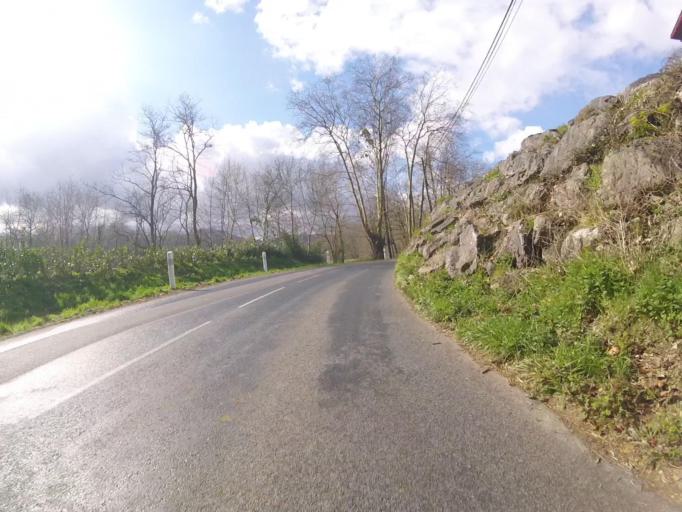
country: FR
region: Aquitaine
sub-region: Departement des Pyrenees-Atlantiques
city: Sare
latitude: 43.2986
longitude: -1.5722
